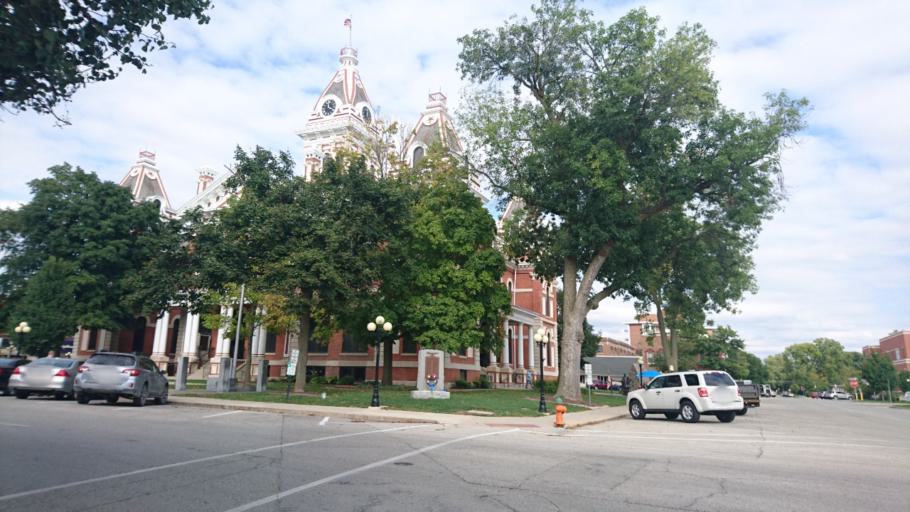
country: US
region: Illinois
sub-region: Livingston County
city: Pontiac
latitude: 40.8795
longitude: -88.6298
